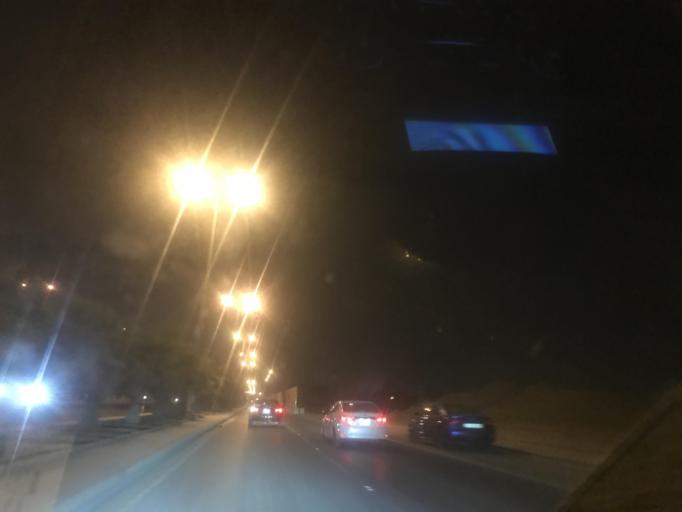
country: SA
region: Ar Riyad
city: Riyadh
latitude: 24.7928
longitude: 46.5874
